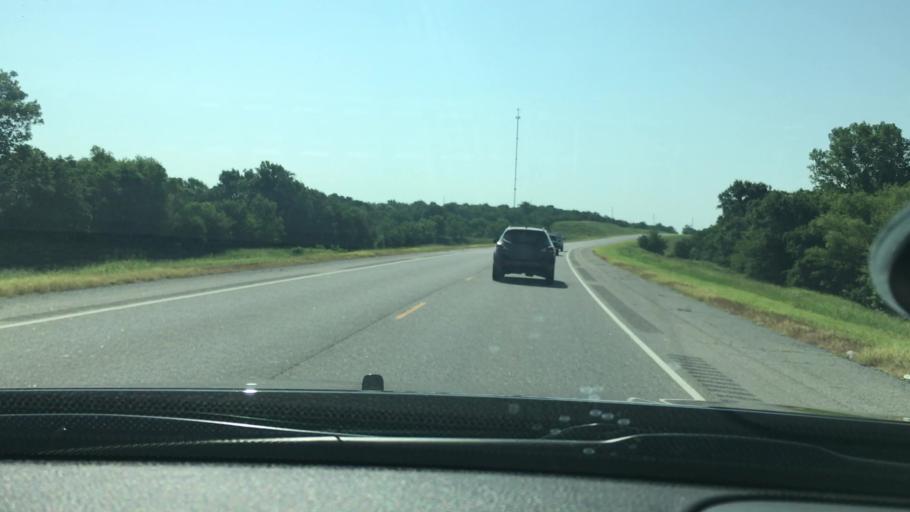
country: US
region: Oklahoma
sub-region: Pontotoc County
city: Ada
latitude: 34.6410
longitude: -96.4877
